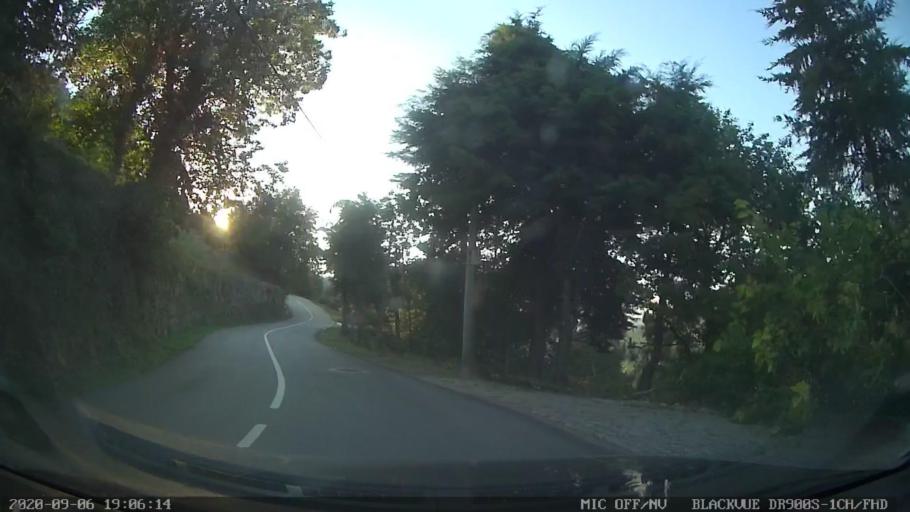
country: PT
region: Porto
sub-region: Baiao
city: Baiao
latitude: 41.2264
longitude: -7.9985
